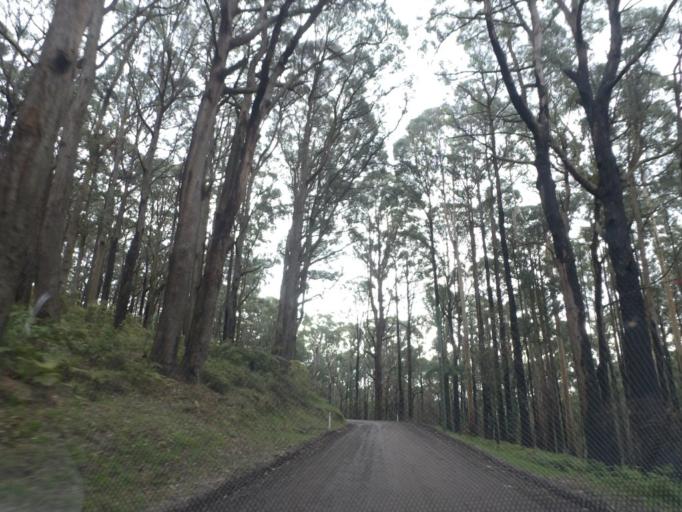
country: AU
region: Victoria
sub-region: Yarra Ranges
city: Olinda
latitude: -37.8541
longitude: 145.3562
